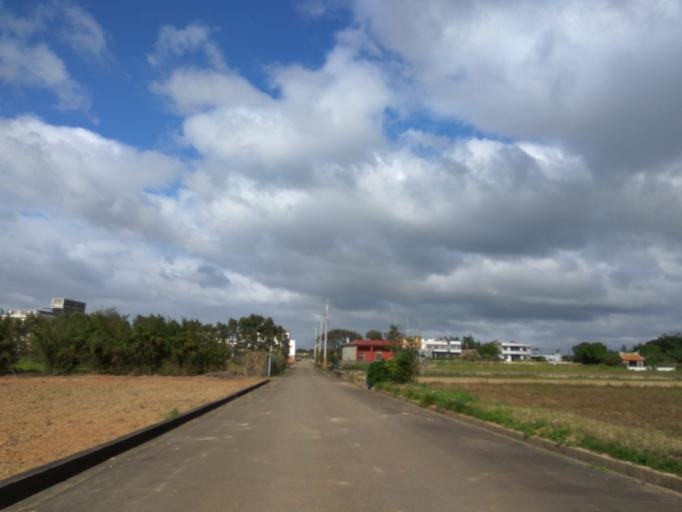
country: TW
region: Taiwan
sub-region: Hsinchu
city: Zhubei
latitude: 24.9696
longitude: 121.0882
